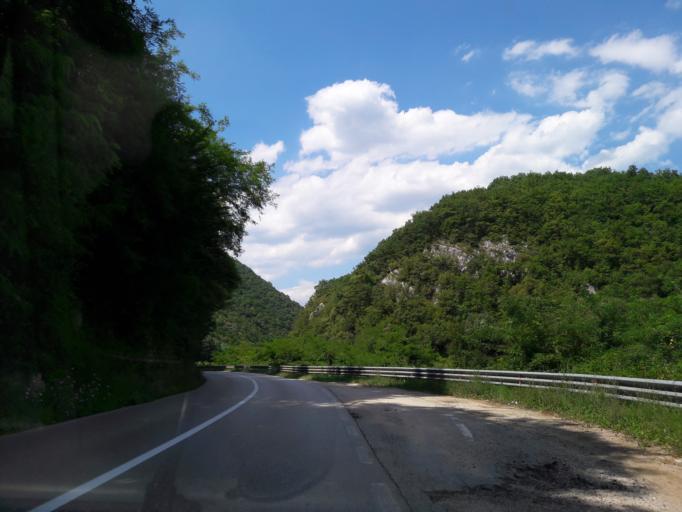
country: BA
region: Republika Srpska
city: Mrkonjic Grad
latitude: 44.5420
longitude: 17.1461
